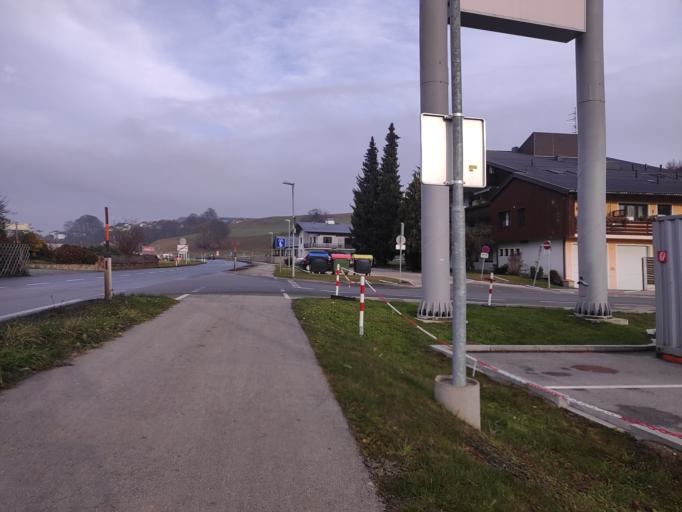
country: AT
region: Salzburg
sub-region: Politischer Bezirk Salzburg-Umgebung
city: Strasswalchen
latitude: 47.9831
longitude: 13.2540
